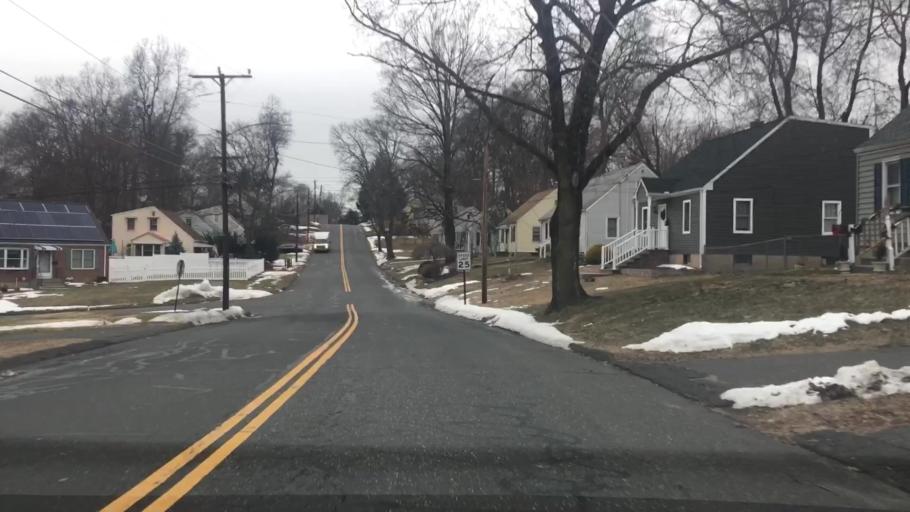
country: US
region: Connecticut
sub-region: Hartford County
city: Bristol
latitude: 41.6798
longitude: -72.9153
